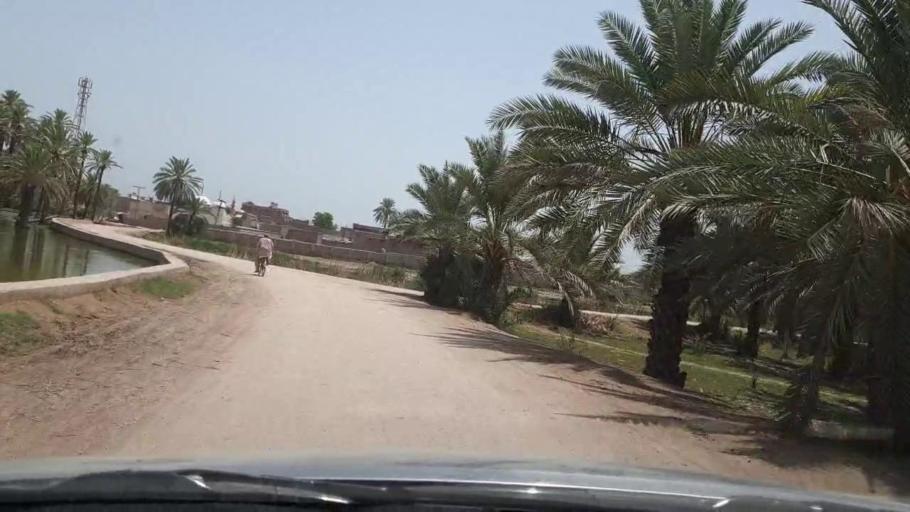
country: PK
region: Sindh
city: Pano Aqil
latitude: 27.8593
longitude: 69.0675
